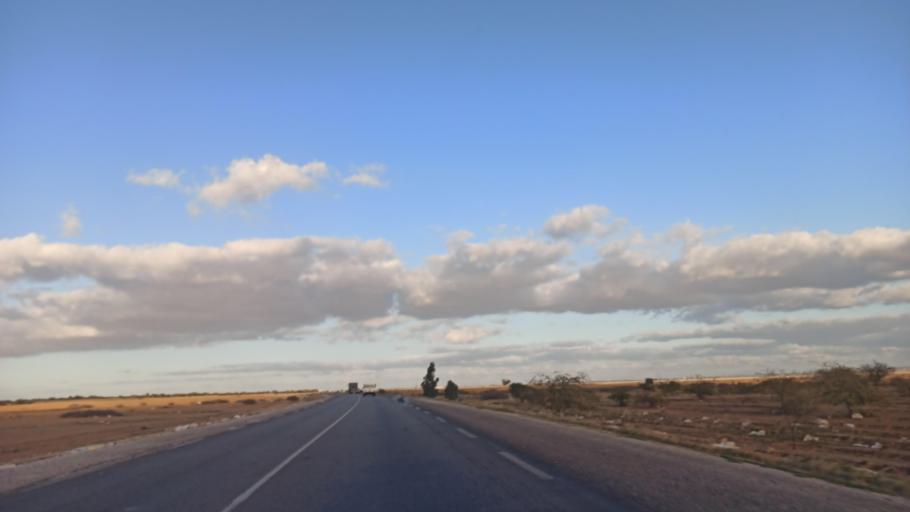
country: TN
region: Susah
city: Sidi Bou Ali
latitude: 35.8943
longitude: 10.2518
